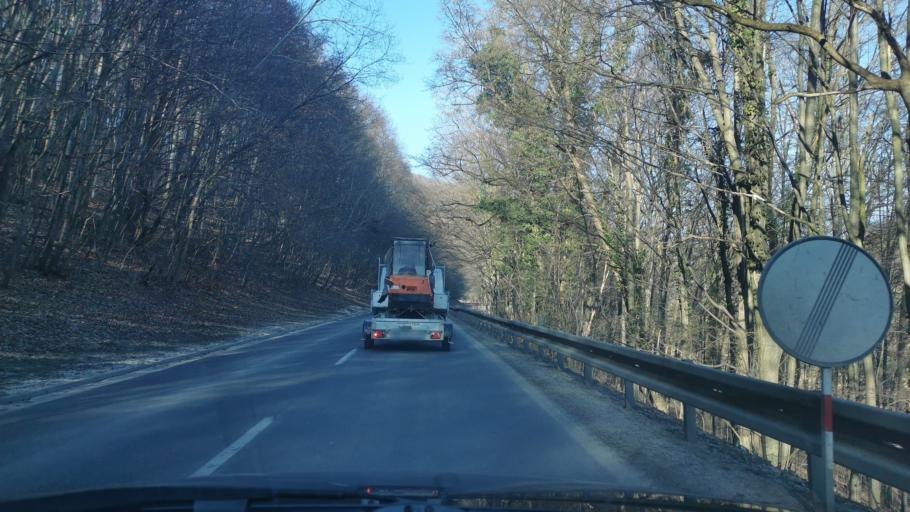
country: SK
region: Trenciansky
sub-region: Okres Myjava
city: Myjava
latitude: 48.7474
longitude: 17.4858
